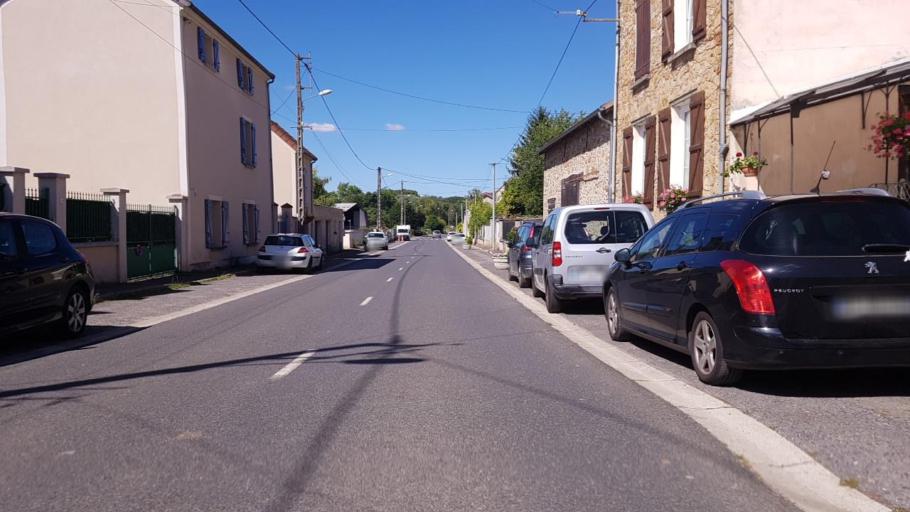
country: FR
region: Ile-de-France
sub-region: Departement de Seine-et-Marne
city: Saacy-sur-Marne
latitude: 48.9788
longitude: 3.2366
